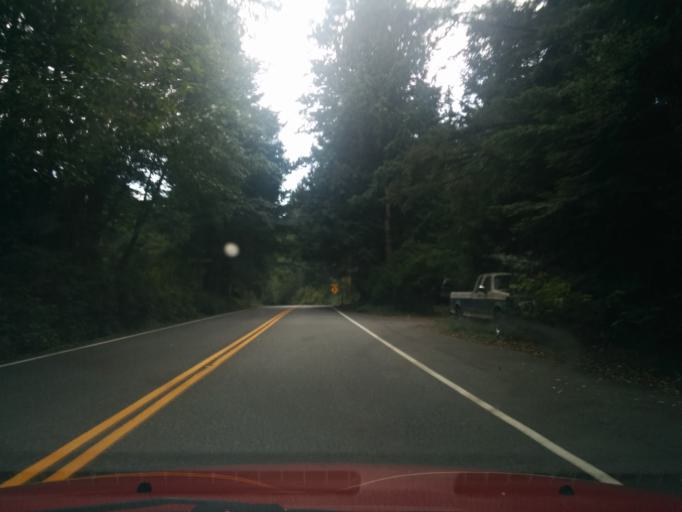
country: US
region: Washington
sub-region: Whatcom County
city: Bellingham
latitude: 48.6644
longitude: -122.4904
